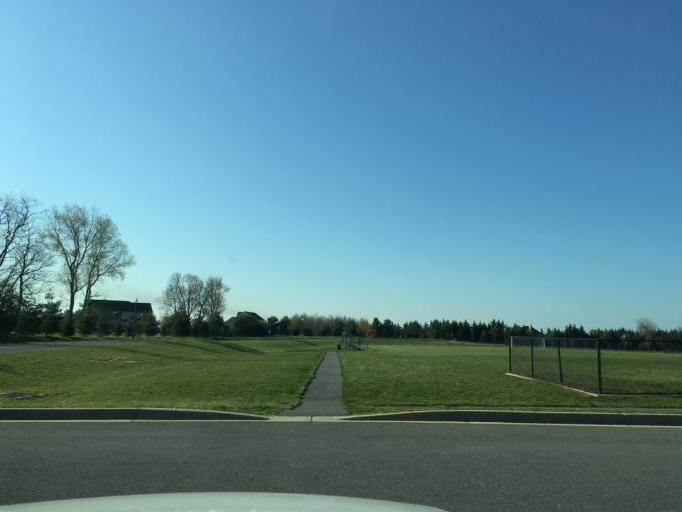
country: US
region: Maryland
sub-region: Frederick County
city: Walkersville
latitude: 39.5141
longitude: -77.4007
